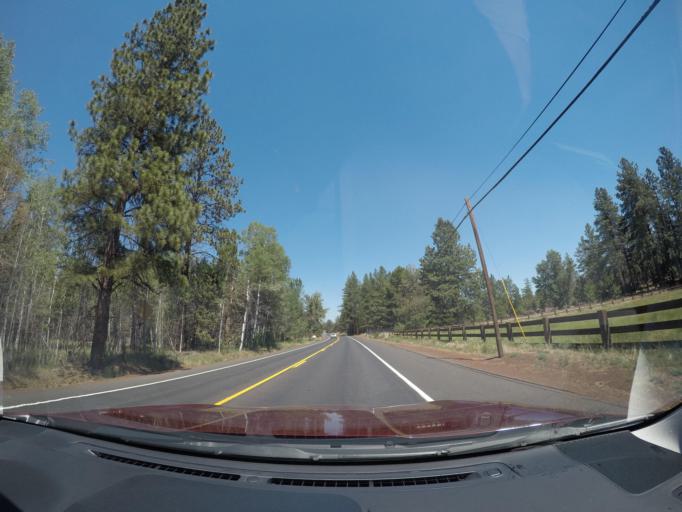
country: US
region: Oregon
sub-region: Deschutes County
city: Sisters
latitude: 44.2865
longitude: -121.5146
